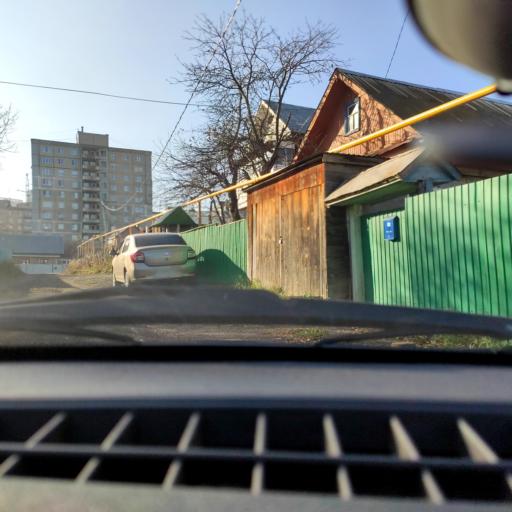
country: RU
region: Bashkortostan
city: Ufa
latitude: 54.7790
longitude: 56.0405
